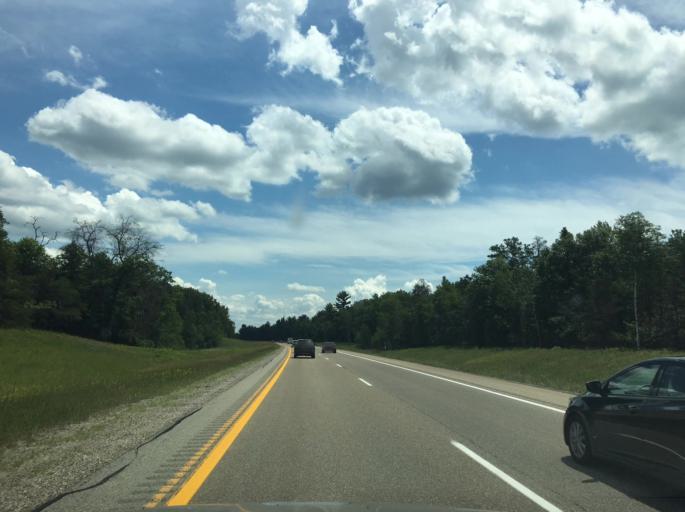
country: US
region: Michigan
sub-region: Crawford County
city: Grayling
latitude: 44.5517
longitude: -84.7045
